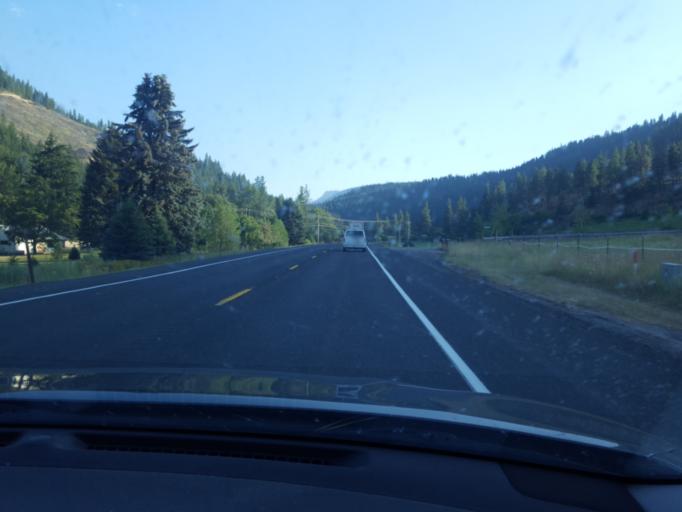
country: US
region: Washington
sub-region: Chelan County
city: Leavenworth
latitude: 47.5156
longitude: -120.6282
